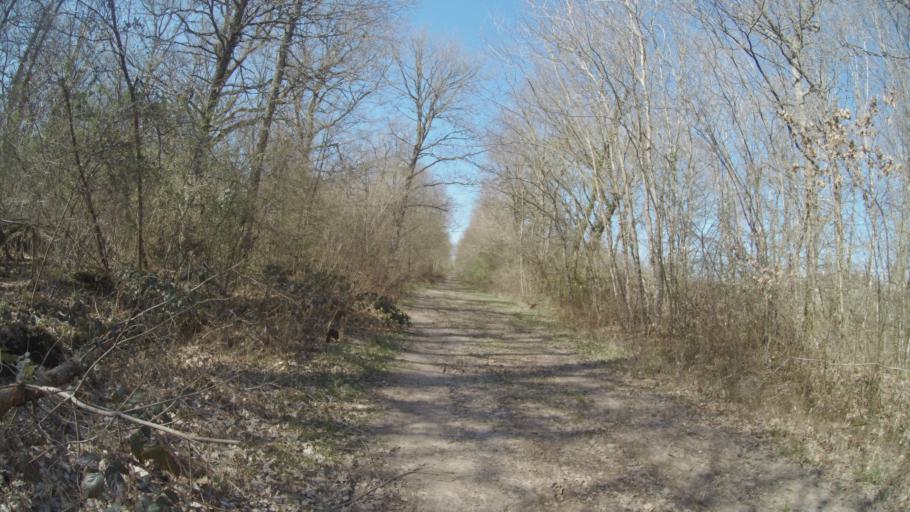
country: FR
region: Centre
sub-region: Departement du Loiret
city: Chanteau
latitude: 47.9536
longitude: 1.9782
